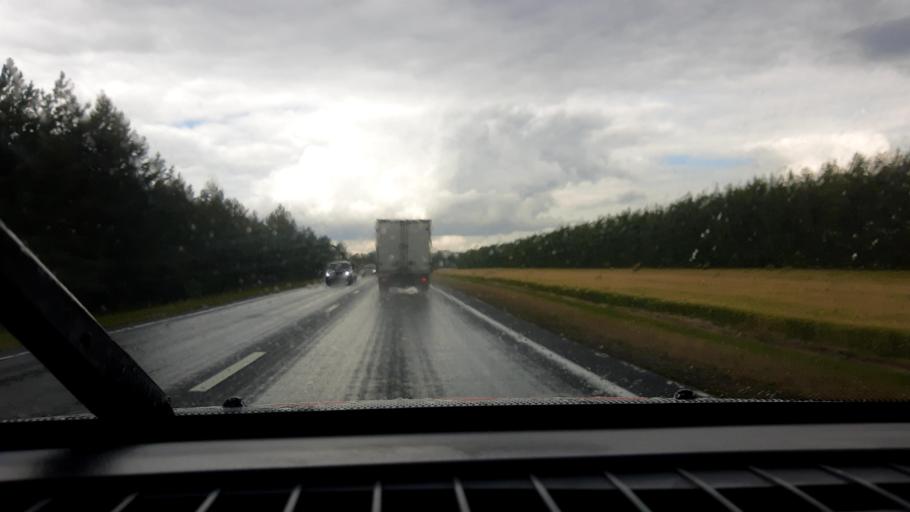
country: RU
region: Nizjnij Novgorod
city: Bol'shoye Murashkino
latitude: 55.9062
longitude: 44.7076
